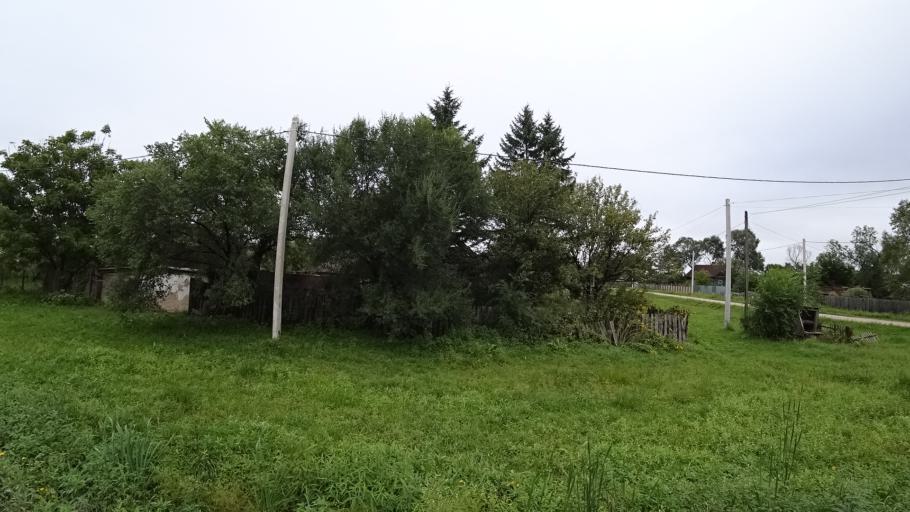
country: RU
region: Primorskiy
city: Monastyrishche
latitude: 44.0788
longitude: 132.5843
